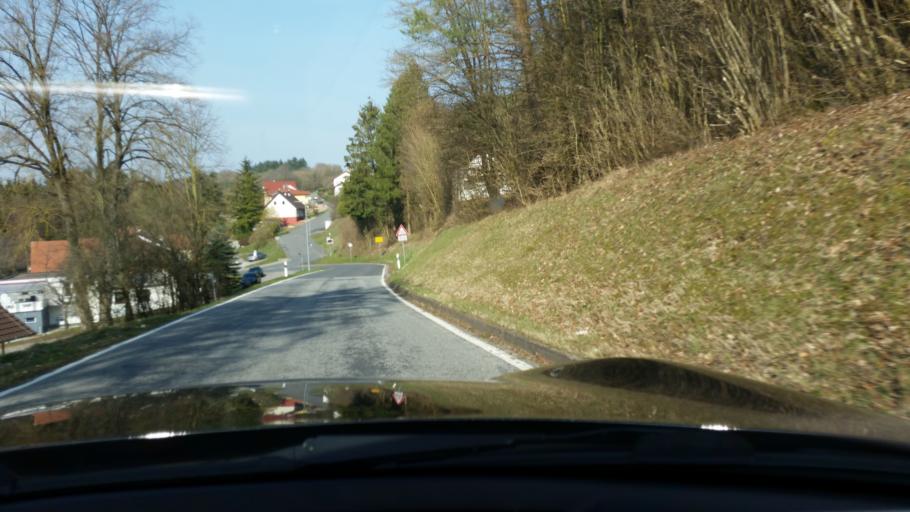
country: DE
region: Baden-Wuerttemberg
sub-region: Karlsruhe Region
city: Billigheim
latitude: 49.3721
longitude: 9.2679
